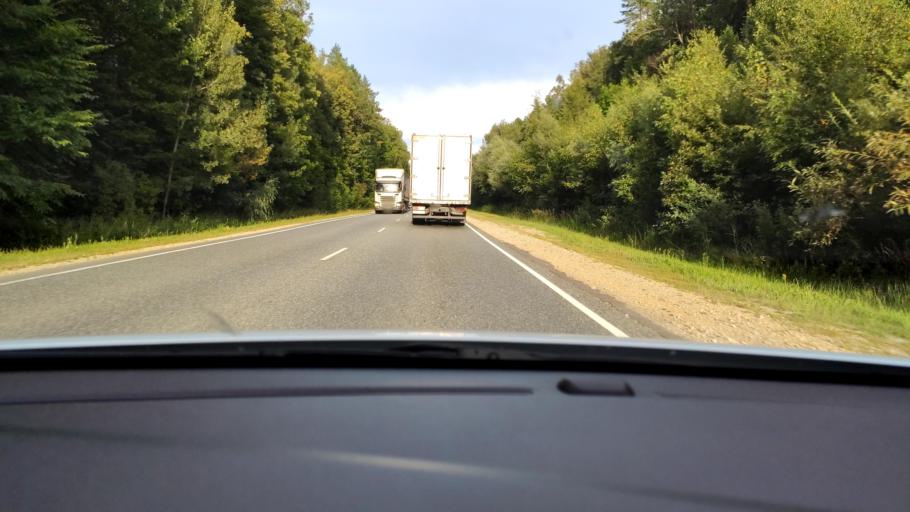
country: RU
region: Tatarstan
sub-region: Zelenodol'skiy Rayon
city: Zelenodolsk
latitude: 55.8837
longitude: 48.4871
